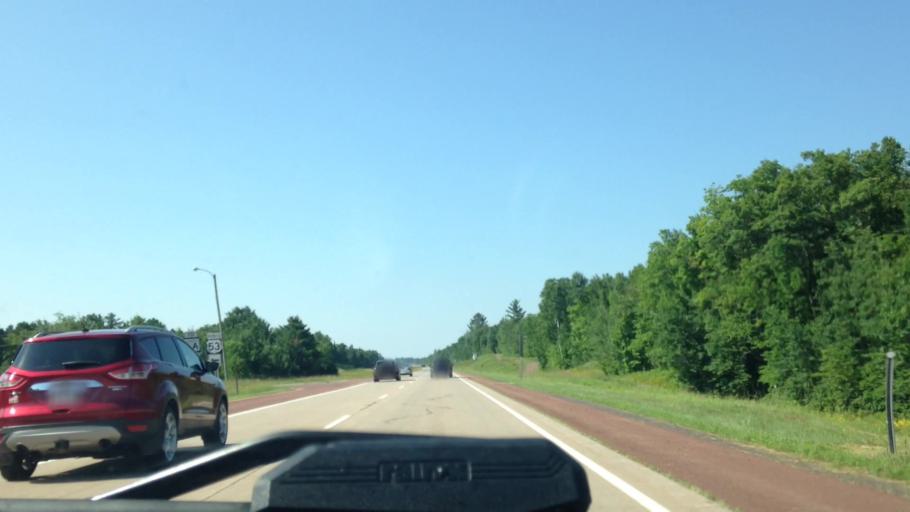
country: US
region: Wisconsin
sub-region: Douglas County
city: Lake Nebagamon
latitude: 46.3823
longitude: -91.8228
